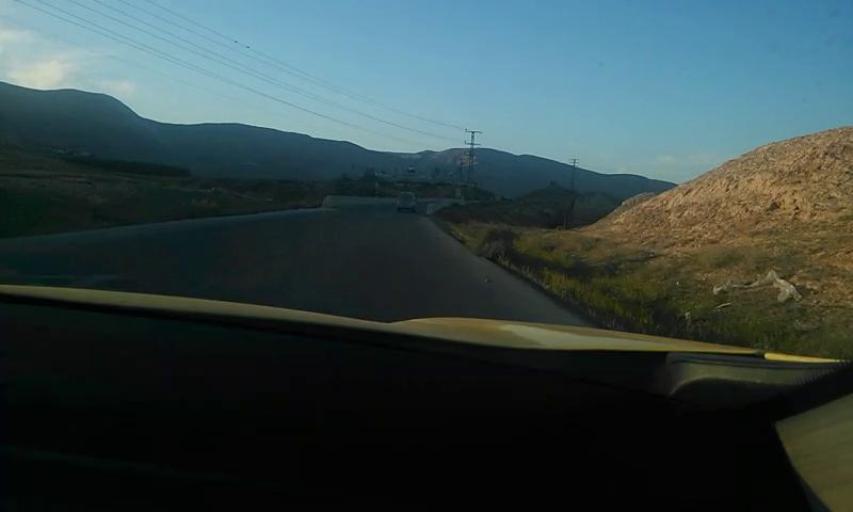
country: PS
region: West Bank
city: An Nuway`imah
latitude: 31.9090
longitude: 35.4230
